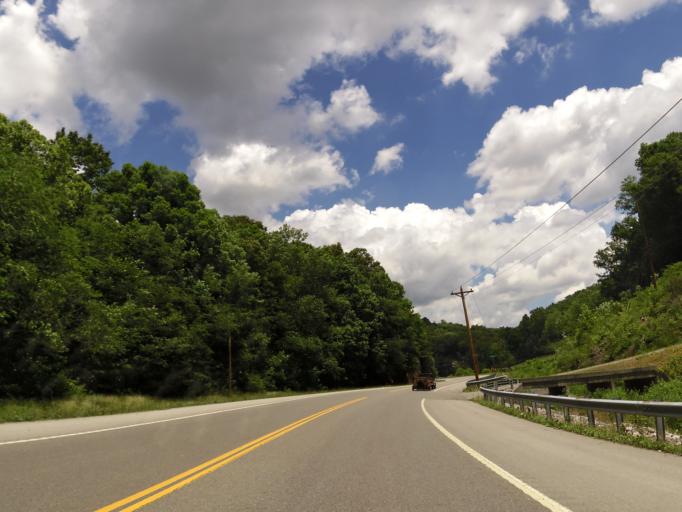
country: US
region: Tennessee
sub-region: Claiborne County
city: New Tazewell
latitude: 36.3869
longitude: -83.7089
